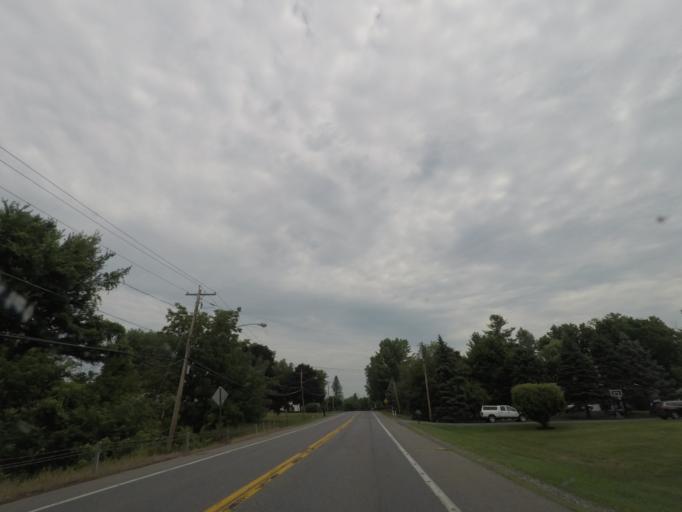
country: US
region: New York
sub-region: Saratoga County
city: Waterford
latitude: 42.8075
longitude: -73.6844
